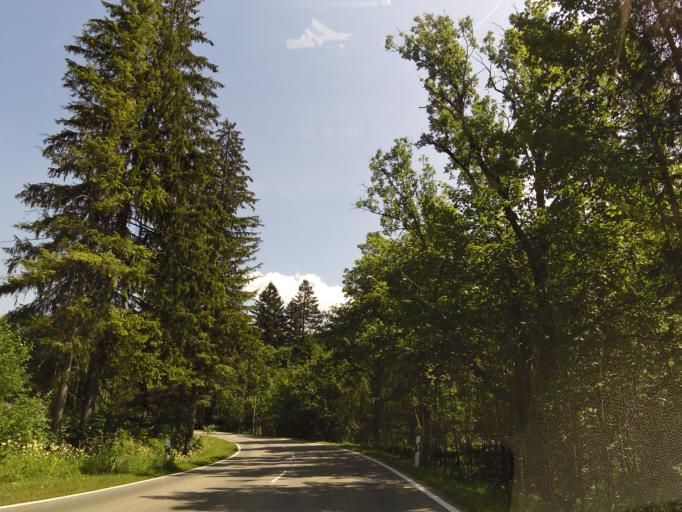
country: DE
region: Bavaria
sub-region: Upper Bavaria
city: Reit im Winkl
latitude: 47.6591
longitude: 12.5276
